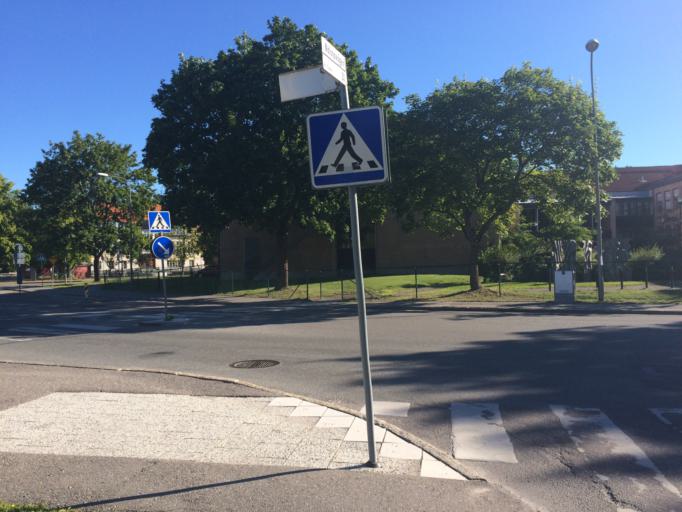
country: SE
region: Stockholm
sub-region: Stockholms Kommun
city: Kista
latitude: 59.3797
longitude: 17.8914
